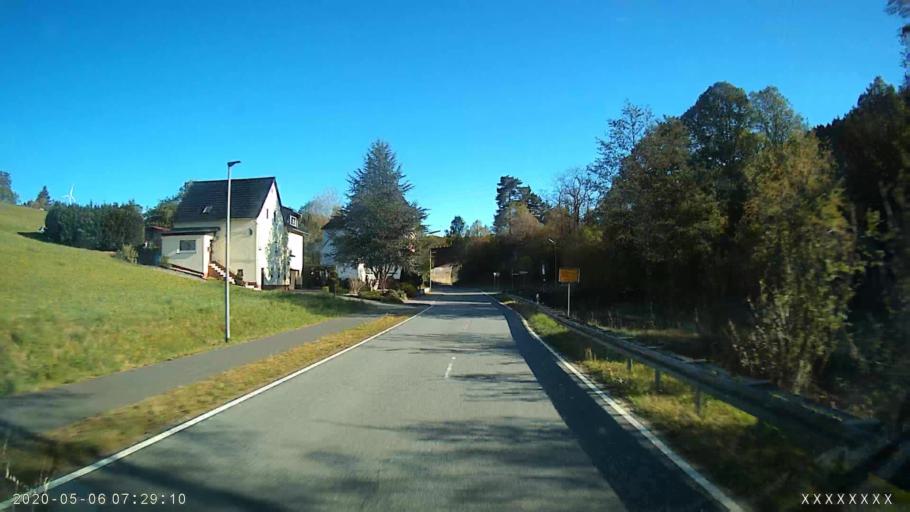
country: DE
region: Hesse
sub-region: Regierungsbezirk Giessen
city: Haiger
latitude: 50.8036
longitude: 8.2016
